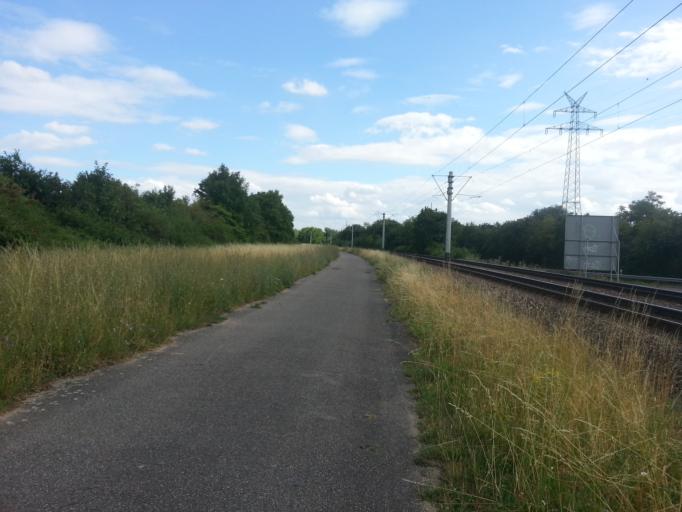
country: DE
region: Baden-Wuerttemberg
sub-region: Karlsruhe Region
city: Ilvesheim
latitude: 49.5033
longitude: 8.5332
